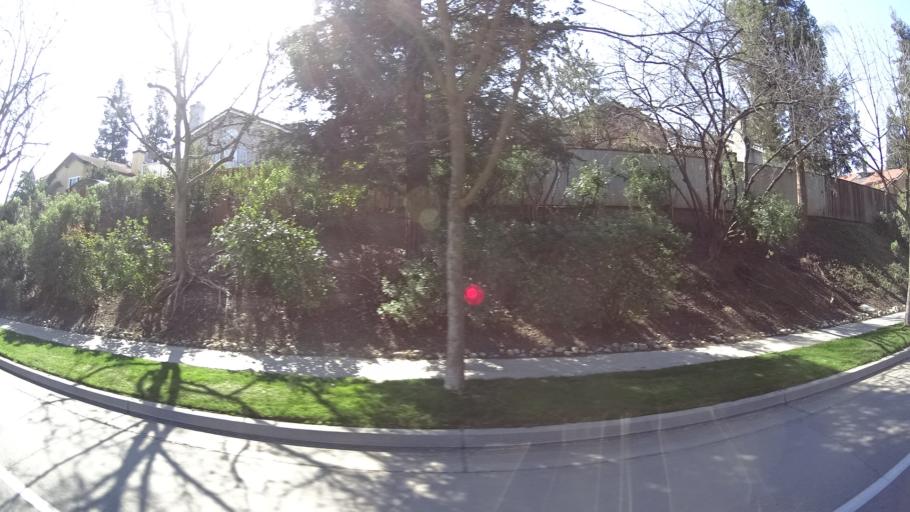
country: US
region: California
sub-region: Fresno County
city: Clovis
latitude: 36.8737
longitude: -119.7664
